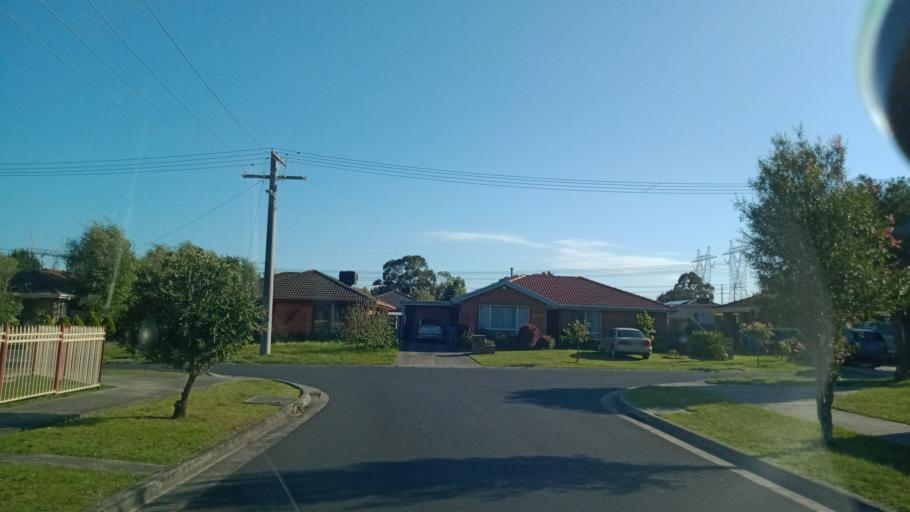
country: AU
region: Victoria
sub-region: Casey
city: Cranbourne West
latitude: -38.0907
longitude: 145.2709
